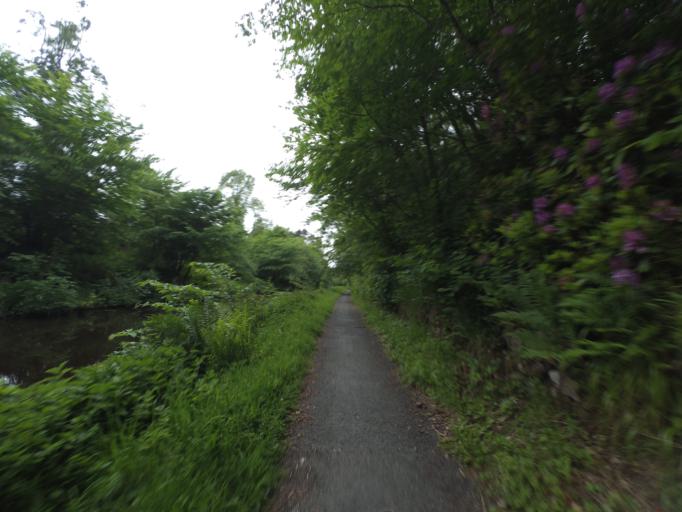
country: GB
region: Scotland
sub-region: West Lothian
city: Broxburn
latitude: 55.9735
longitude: -3.4935
